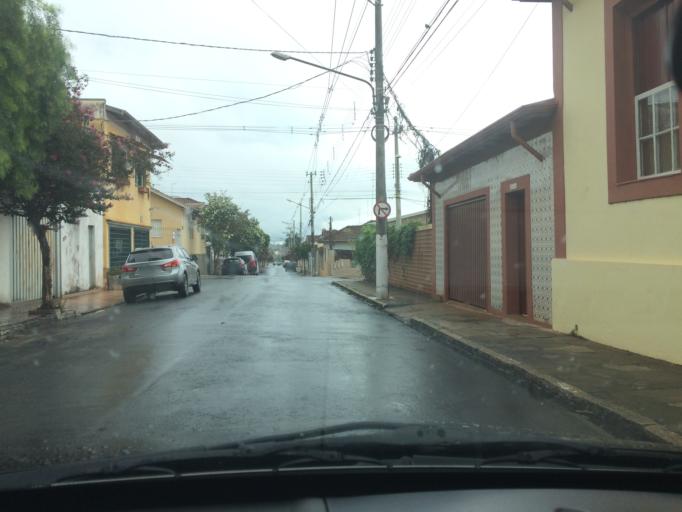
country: BR
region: Sao Paulo
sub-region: Casa Branca
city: Casa Branca
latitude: -21.7720
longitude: -47.0843
